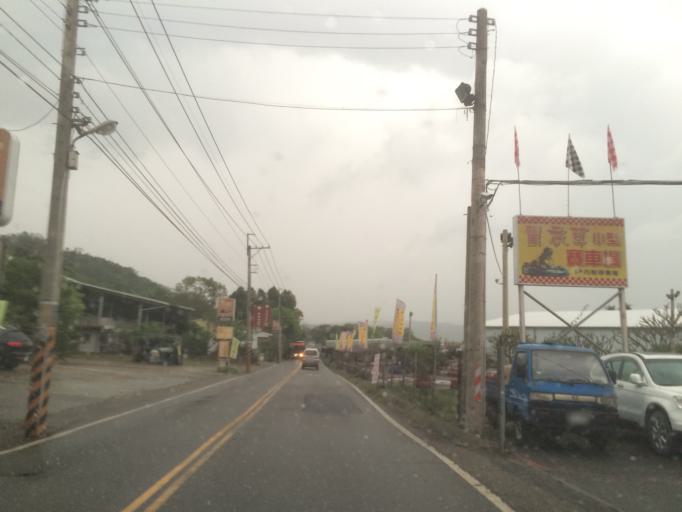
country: TW
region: Taiwan
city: Fengyuan
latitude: 24.1928
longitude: 120.8084
